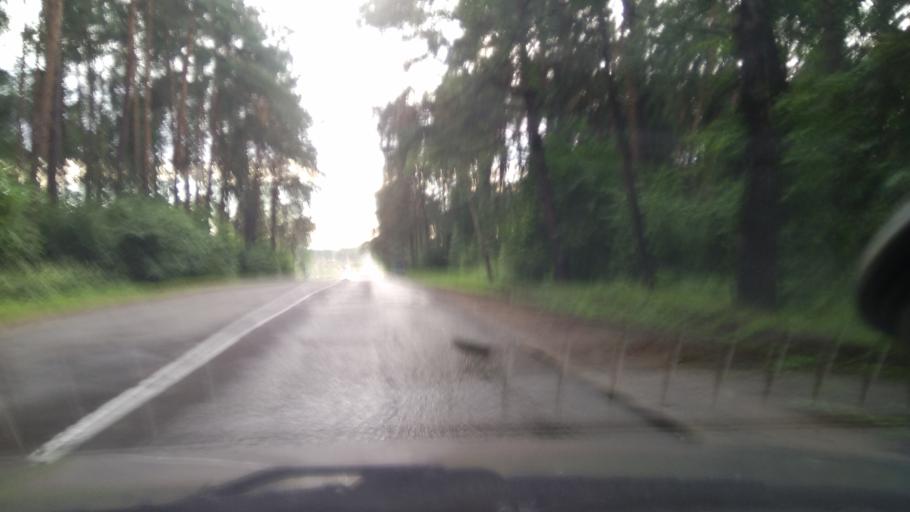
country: BY
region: Minsk
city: Bal'shavik
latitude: 53.9849
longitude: 27.5388
